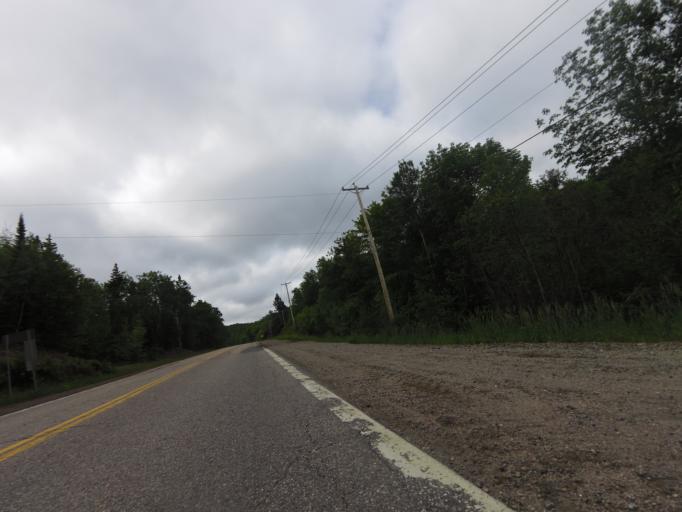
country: CA
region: Quebec
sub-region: Outaouais
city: Shawville
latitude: 45.8346
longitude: -76.4609
